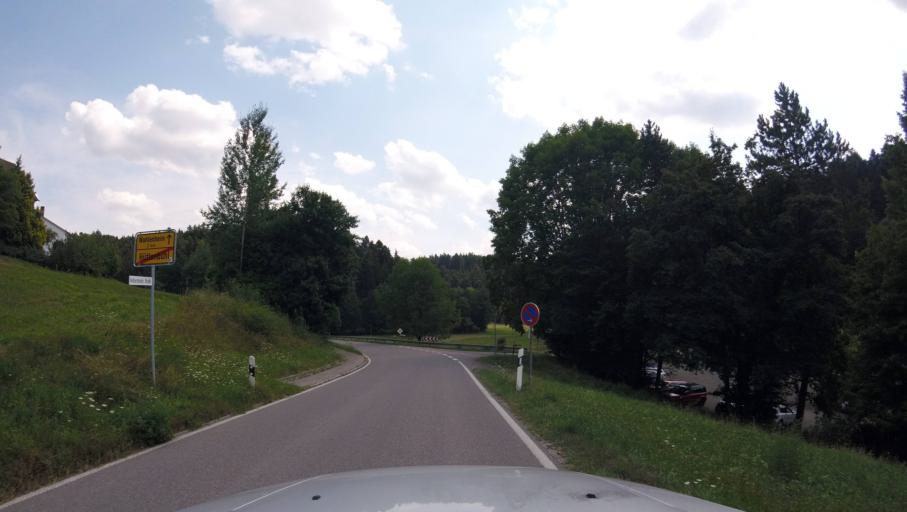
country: DE
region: Baden-Wuerttemberg
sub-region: Regierungsbezirk Stuttgart
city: Alfdorf
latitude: 48.8912
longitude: 9.7008
